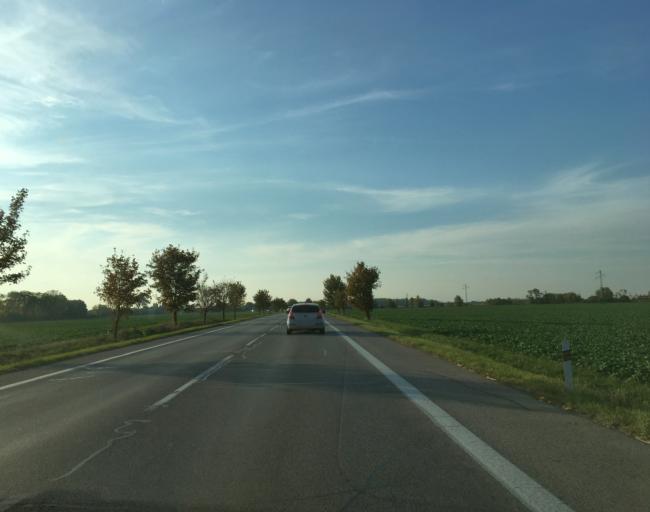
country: SK
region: Nitriansky
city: Sellye
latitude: 48.1497
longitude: 17.9568
